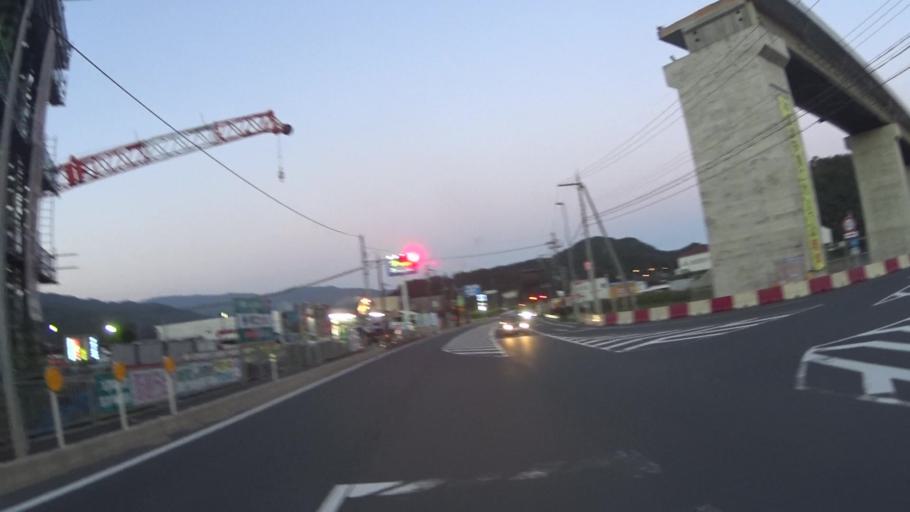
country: JP
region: Kyoto
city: Miyazu
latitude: 35.5511
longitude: 135.1391
